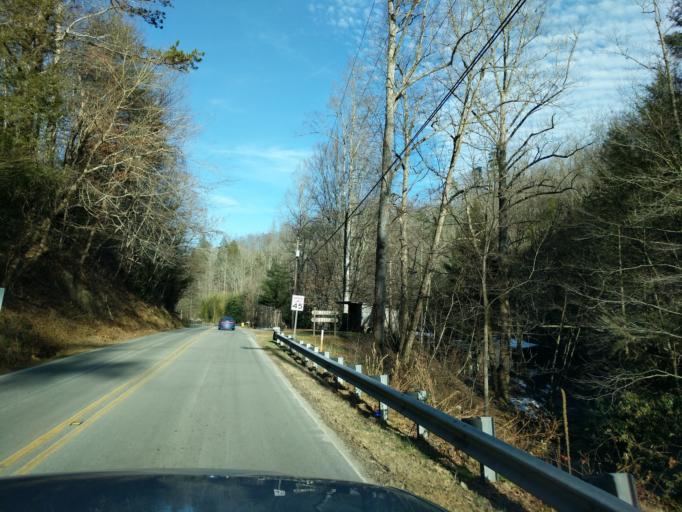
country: US
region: North Carolina
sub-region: Henderson County
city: Edneyville
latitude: 35.4019
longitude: -82.3244
